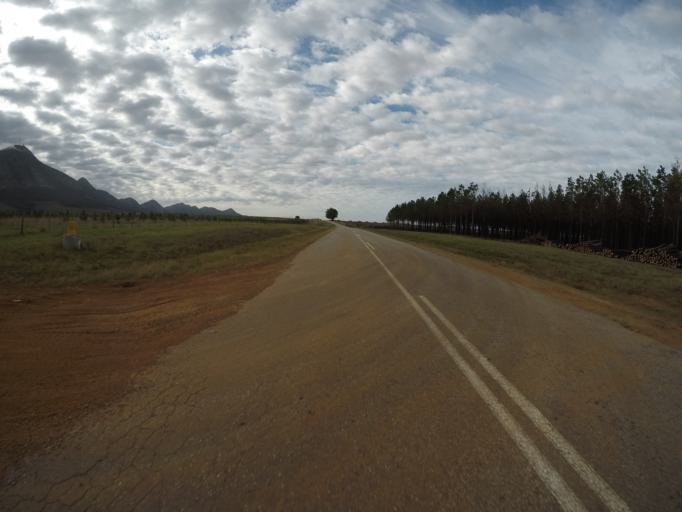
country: ZA
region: Eastern Cape
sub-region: Cacadu District Municipality
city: Kareedouw
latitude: -34.0397
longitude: 24.4046
